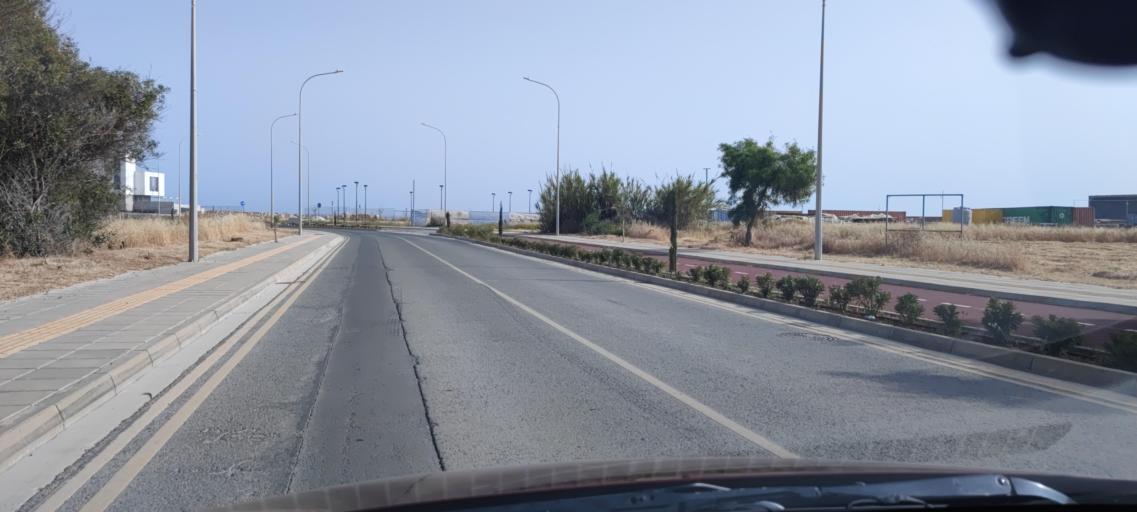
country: CY
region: Ammochostos
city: Liopetri
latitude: 34.9806
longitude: 33.9393
